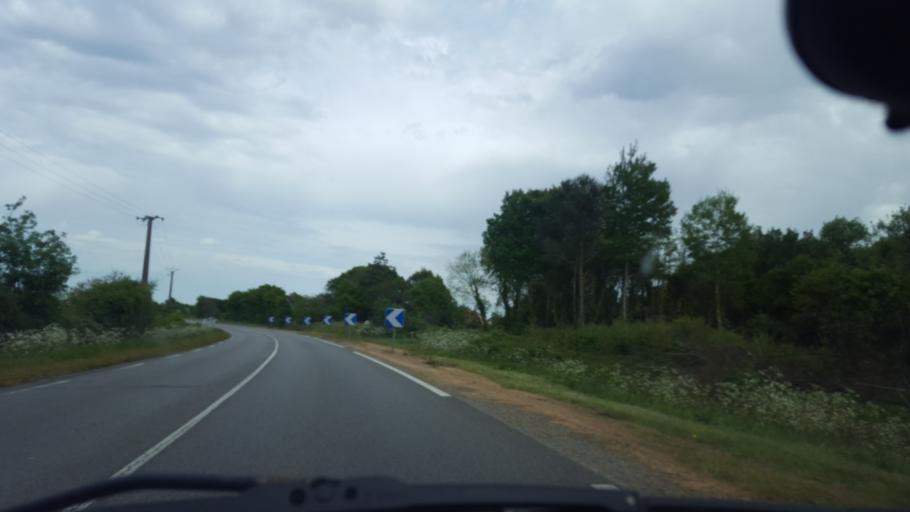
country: FR
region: Pays de la Loire
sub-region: Departement de la Loire-Atlantique
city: Paulx
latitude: 46.9942
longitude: -1.7511
